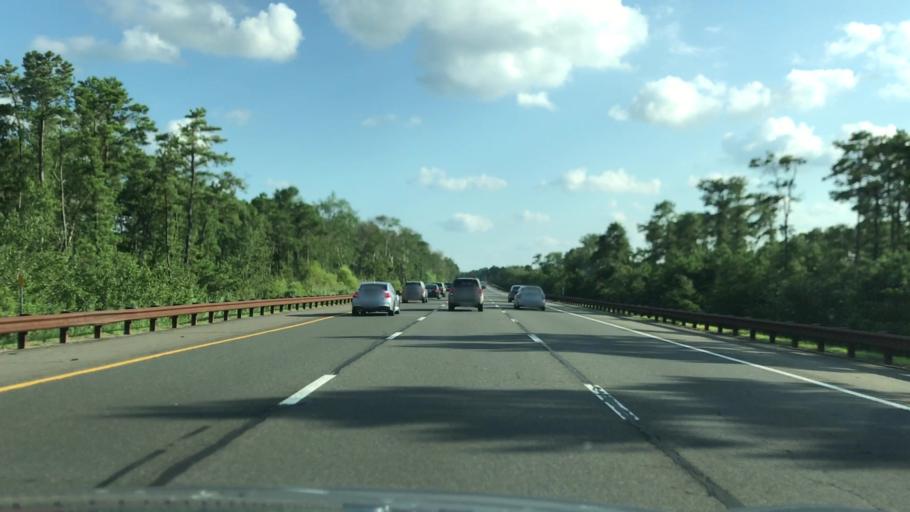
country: US
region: New Jersey
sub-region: Ocean County
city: South Toms River
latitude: 39.9226
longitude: -74.2100
